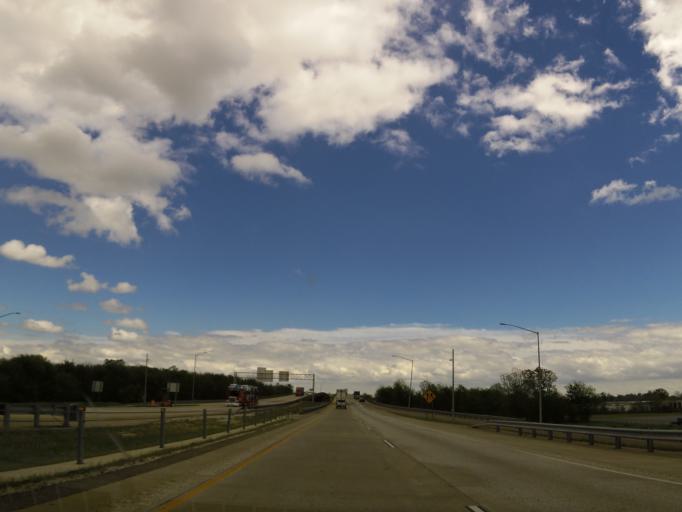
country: US
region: Arkansas
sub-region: Crittenden County
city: West Memphis
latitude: 35.1562
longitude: -90.1351
